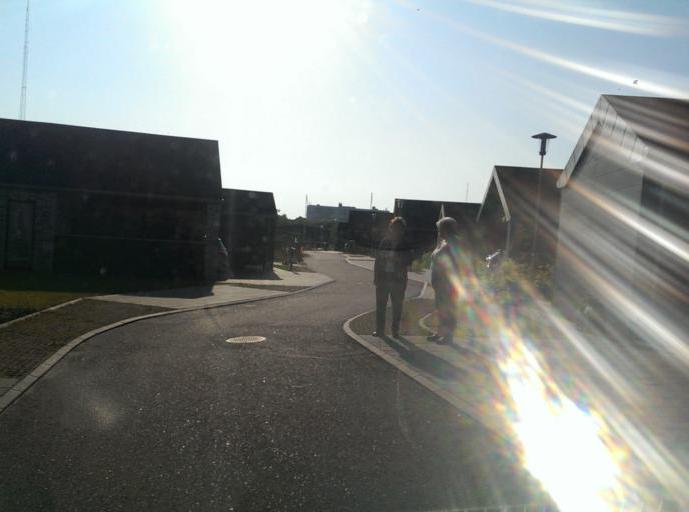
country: DK
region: South Denmark
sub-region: Esbjerg Kommune
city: Esbjerg
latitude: 55.4965
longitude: 8.4572
